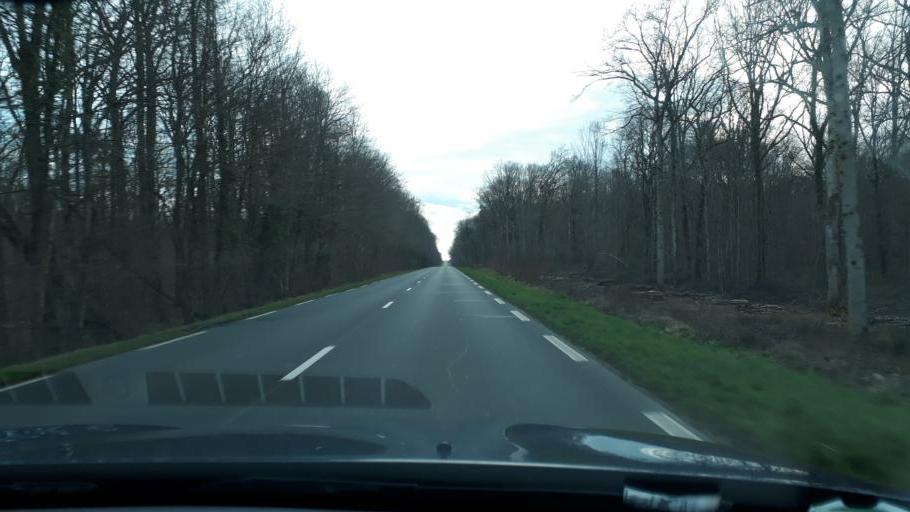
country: FR
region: Centre
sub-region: Departement du Loiret
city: Chilleurs-aux-Bois
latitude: 48.0495
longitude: 2.1267
